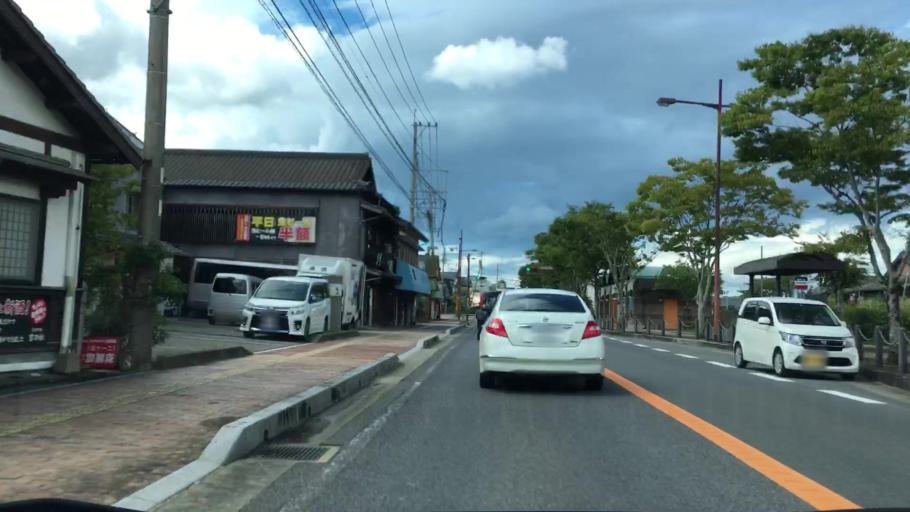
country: JP
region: Saga Prefecture
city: Imaricho-ko
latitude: 33.2095
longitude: 129.8500
